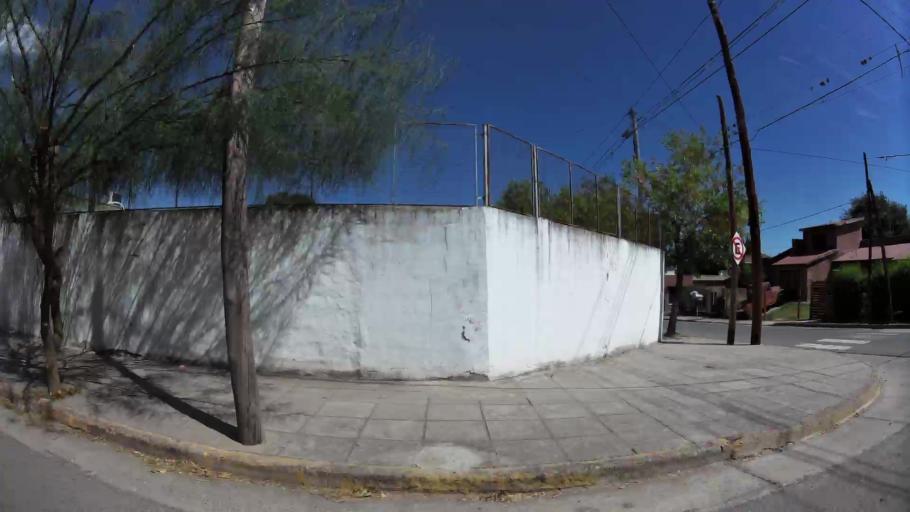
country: AR
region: Cordoba
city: Villa Allende
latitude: -31.2899
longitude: -64.2988
